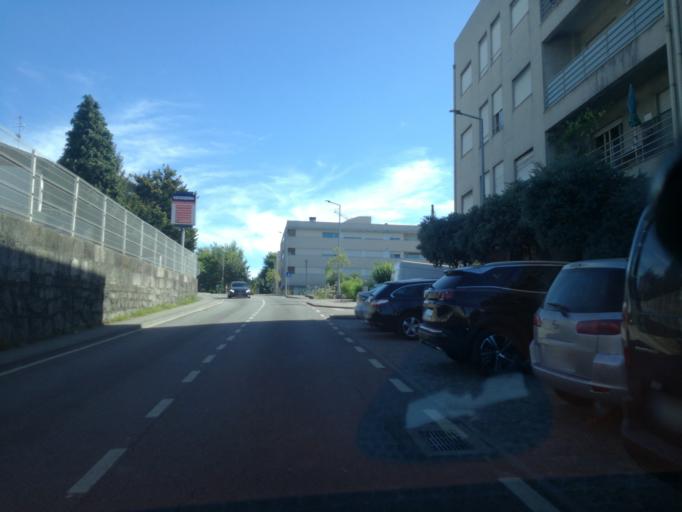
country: PT
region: Braga
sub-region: Guimaraes
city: Guimaraes
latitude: 41.4573
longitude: -8.2961
